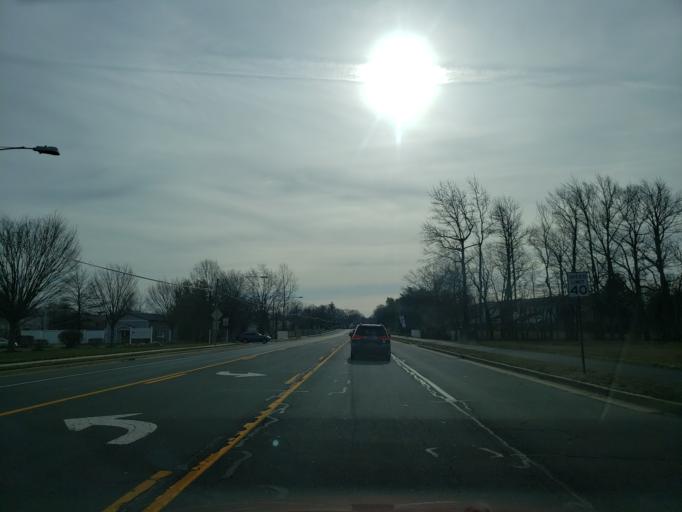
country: US
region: Delaware
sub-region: Kent County
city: Dover
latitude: 39.1752
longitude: -75.5521
